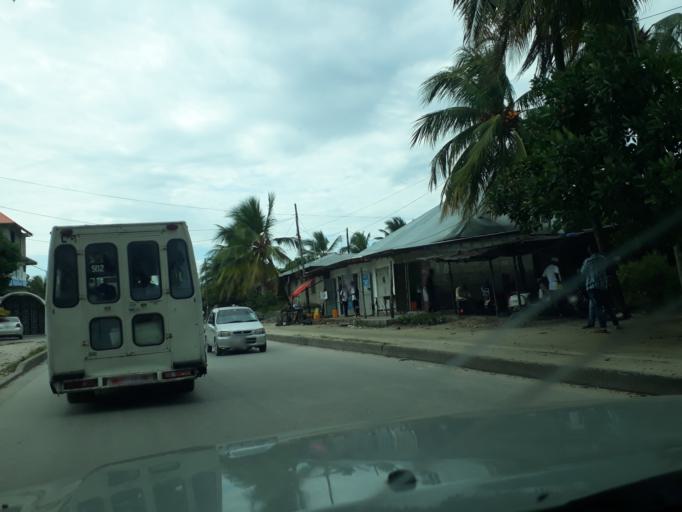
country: TZ
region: Zanzibar Urban/West
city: Zanzibar
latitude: -6.1028
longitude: 39.2179
